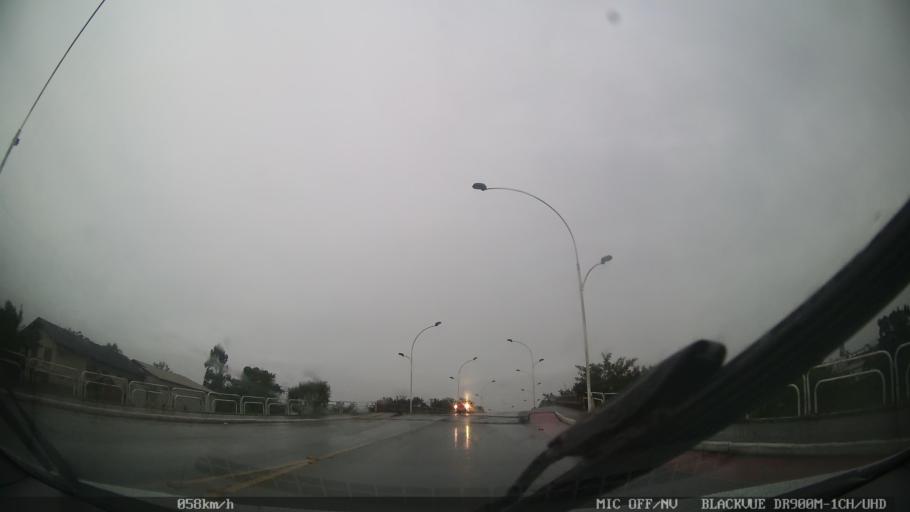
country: BR
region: Santa Catarina
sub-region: Itajai
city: Itajai
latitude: -26.9182
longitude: -48.6875
